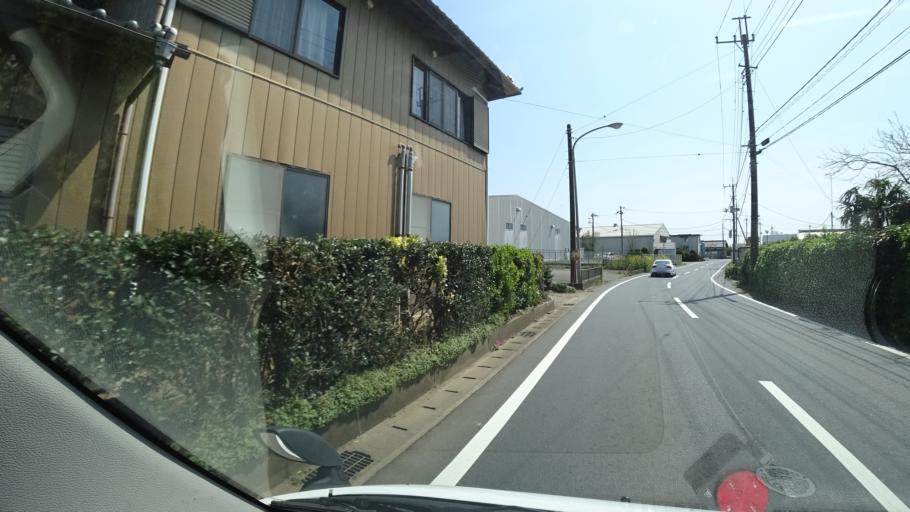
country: JP
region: Chiba
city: Narita
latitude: 35.7253
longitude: 140.3914
